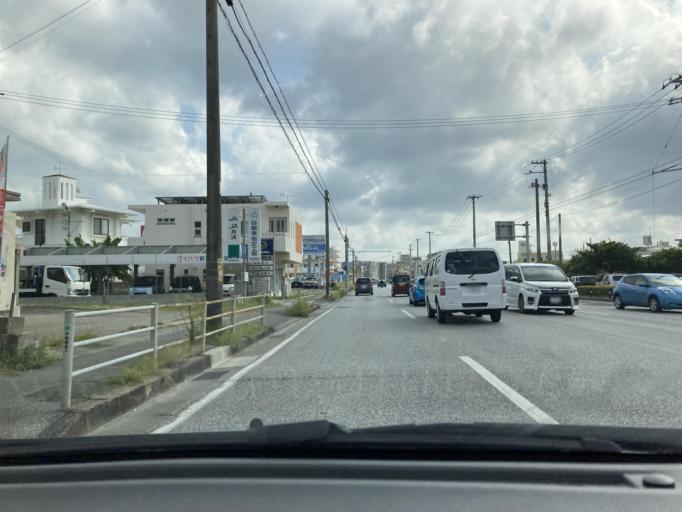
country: JP
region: Okinawa
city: Ginowan
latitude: 26.2240
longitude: 127.7659
